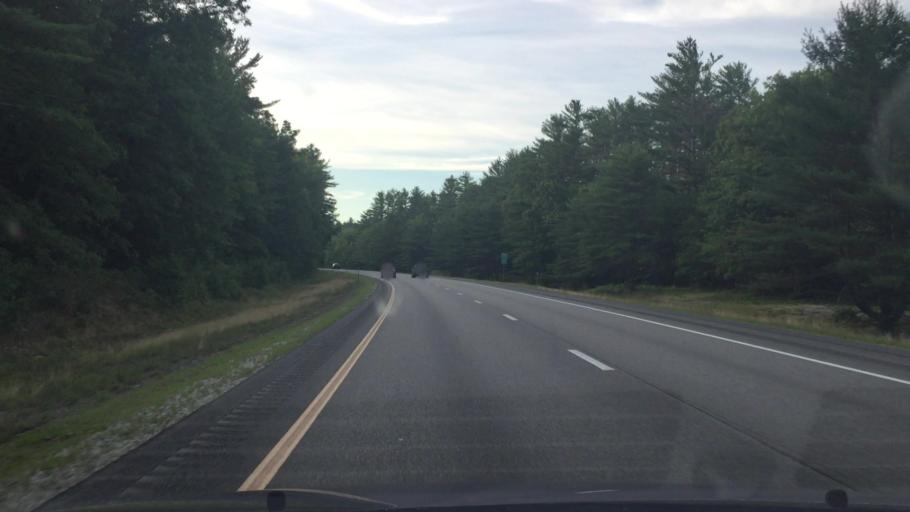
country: US
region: New Hampshire
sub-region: Merrimack County
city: Canterbury
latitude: 43.3098
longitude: -71.5829
